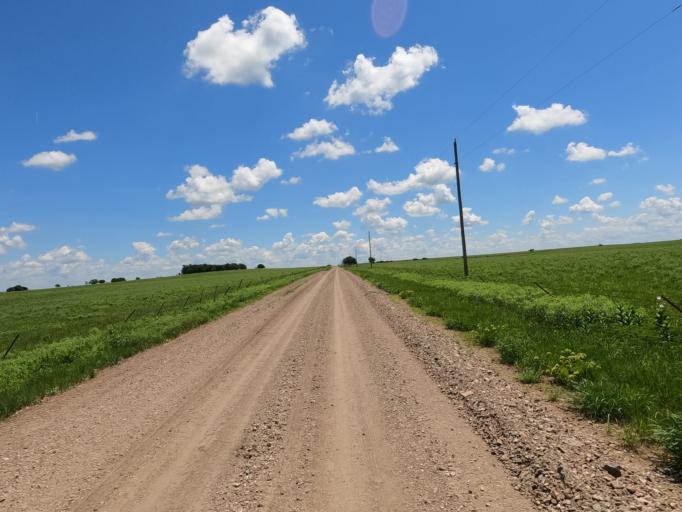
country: US
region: Kansas
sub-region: Chase County
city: Cottonwood Falls
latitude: 38.2167
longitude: -96.7644
